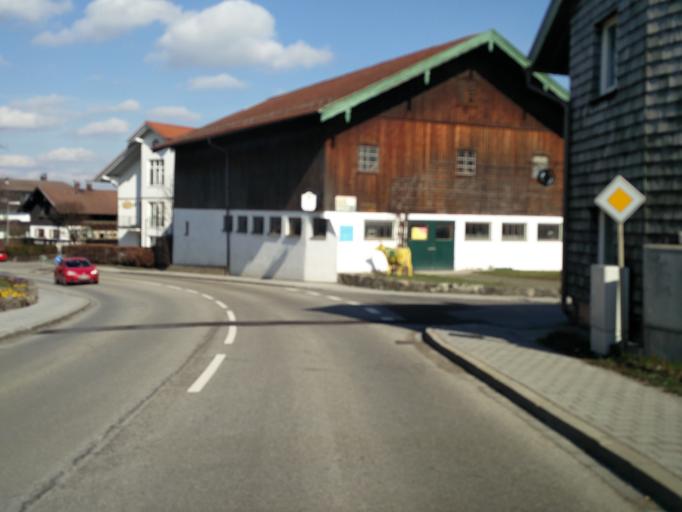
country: DE
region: Bavaria
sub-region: Upper Bavaria
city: Rimsting
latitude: 47.8784
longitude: 12.3379
